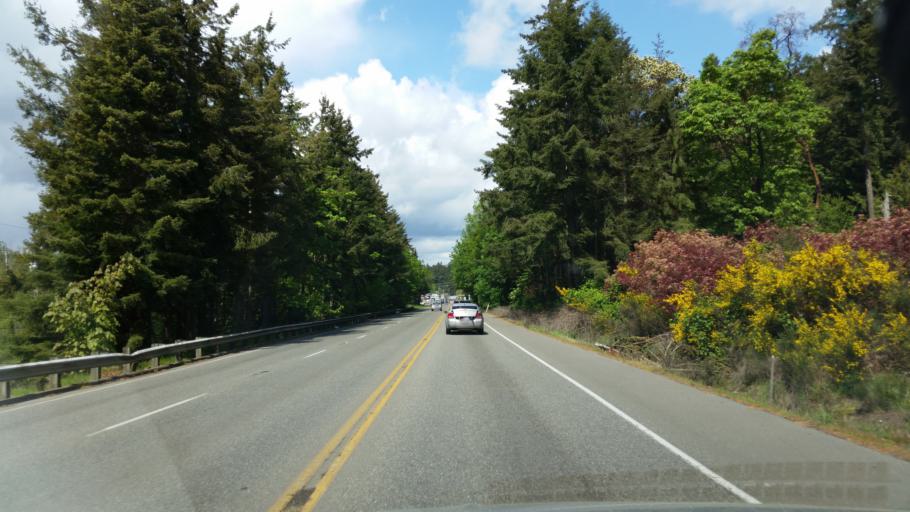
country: US
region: Washington
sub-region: Pierce County
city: Purdy
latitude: 47.3792
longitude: -122.6241
